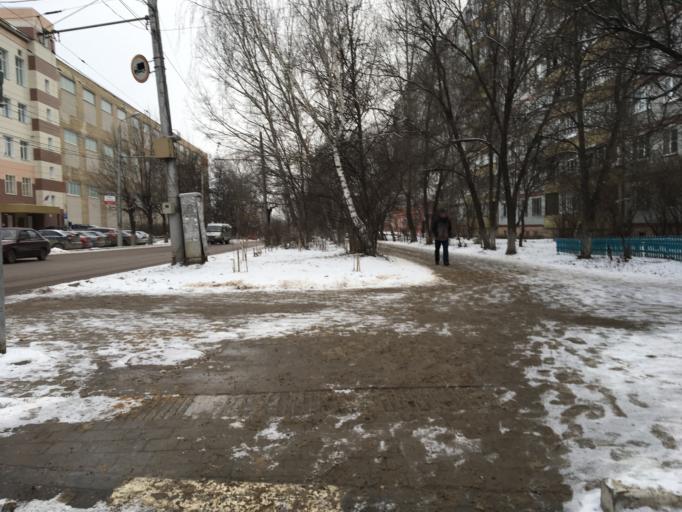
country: RU
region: Tula
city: Tula
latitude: 54.2078
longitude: 37.6084
